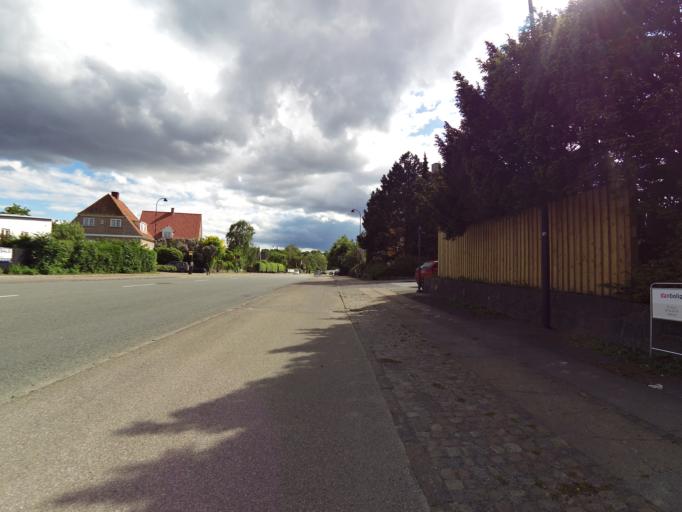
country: DK
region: Capital Region
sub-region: Frederiksberg Kommune
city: Frederiksberg
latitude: 55.7253
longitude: 12.5480
